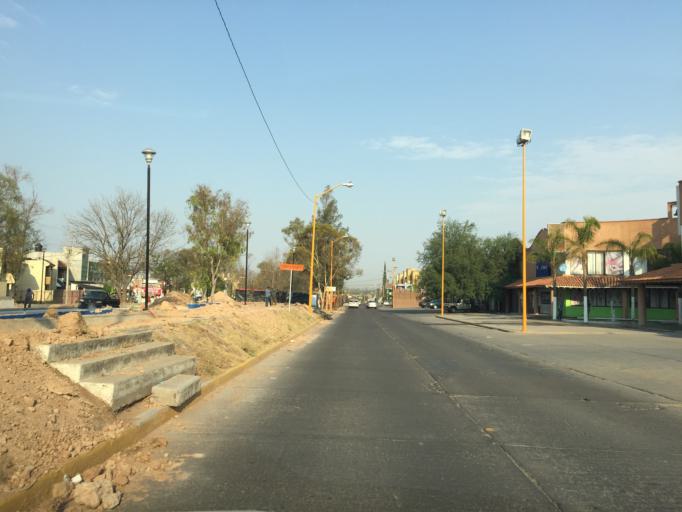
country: MX
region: Aguascalientes
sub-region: Aguascalientes
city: Pocitos
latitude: 21.9029
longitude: -102.3113
